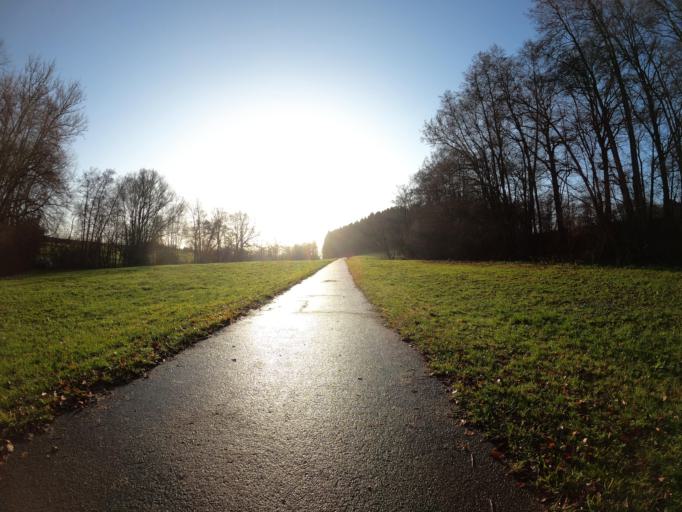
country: DE
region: Baden-Wuerttemberg
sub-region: Regierungsbezirk Stuttgart
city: Uhingen
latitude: 48.6957
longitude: 9.6183
